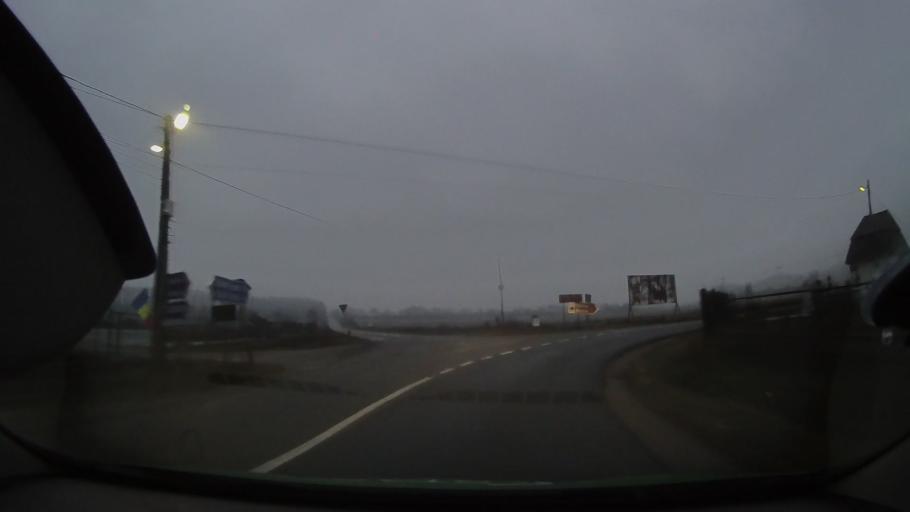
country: RO
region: Arad
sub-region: Comuna Beliu
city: Beliu
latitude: 46.4858
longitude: 21.9965
